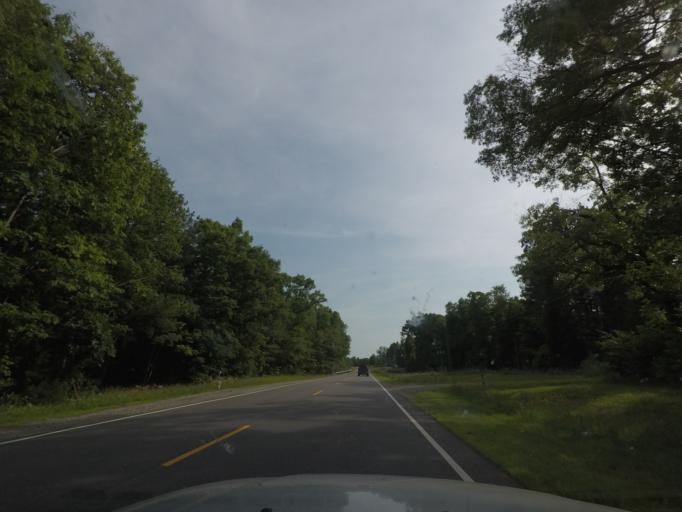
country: US
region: Virginia
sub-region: Mecklenburg County
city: Clarksville
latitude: 36.7715
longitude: -78.6223
